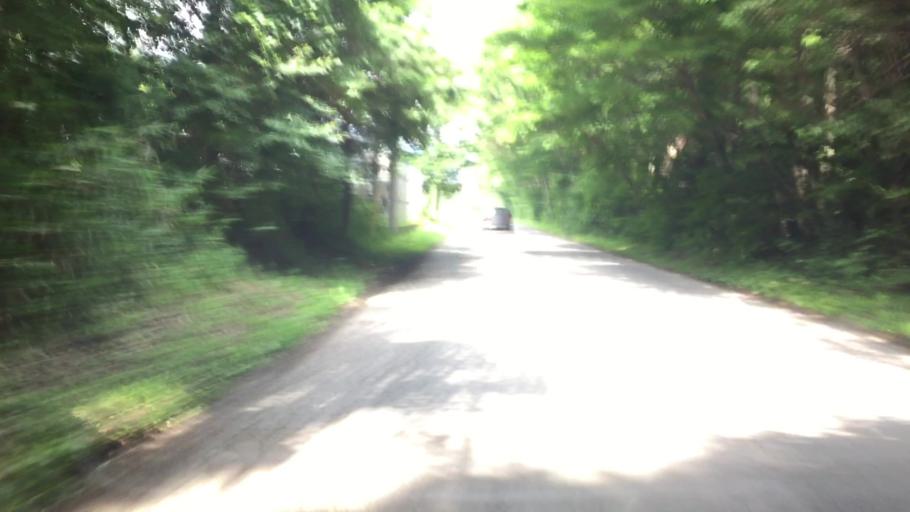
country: JP
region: Tochigi
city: Kuroiso
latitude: 37.0394
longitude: 139.9513
